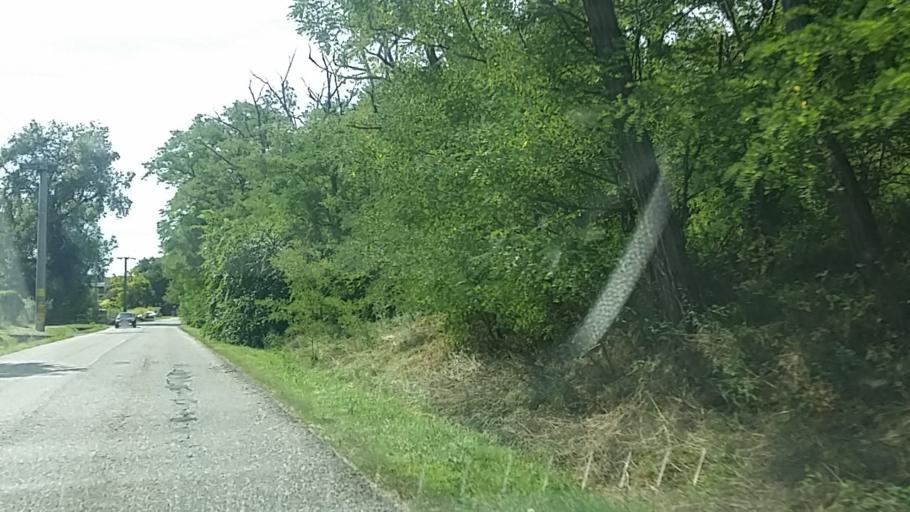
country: HU
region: Pest
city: Szada
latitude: 47.6232
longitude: 19.3011
